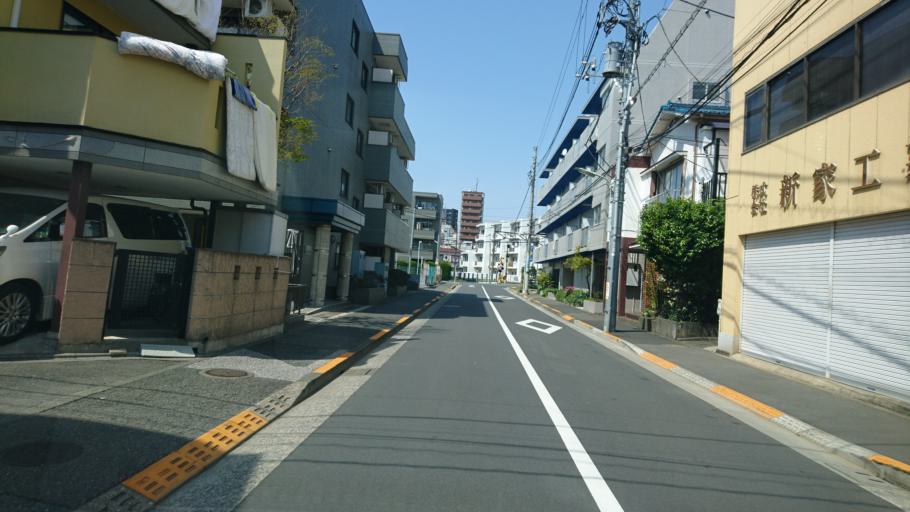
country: JP
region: Kanagawa
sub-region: Kawasaki-shi
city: Kawasaki
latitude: 35.5696
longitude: 139.7056
